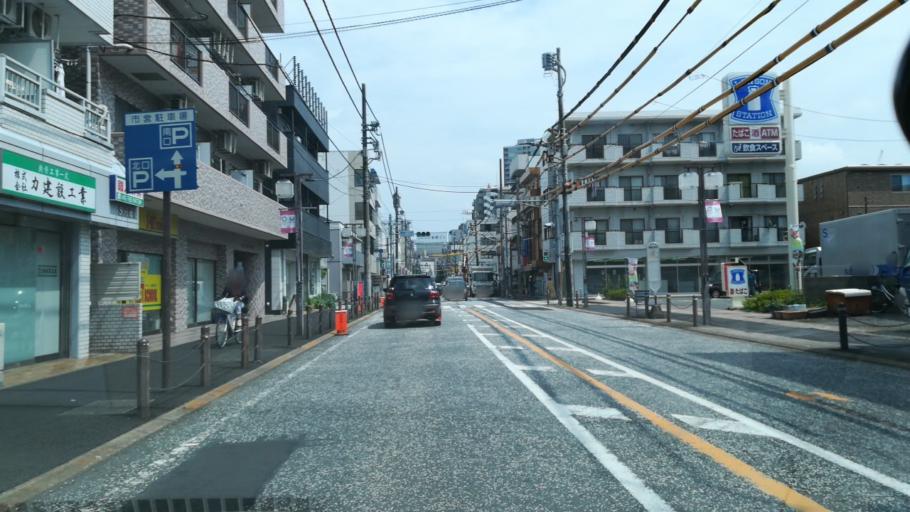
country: JP
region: Tokyo
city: Hachioji
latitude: 35.5816
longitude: 139.3654
